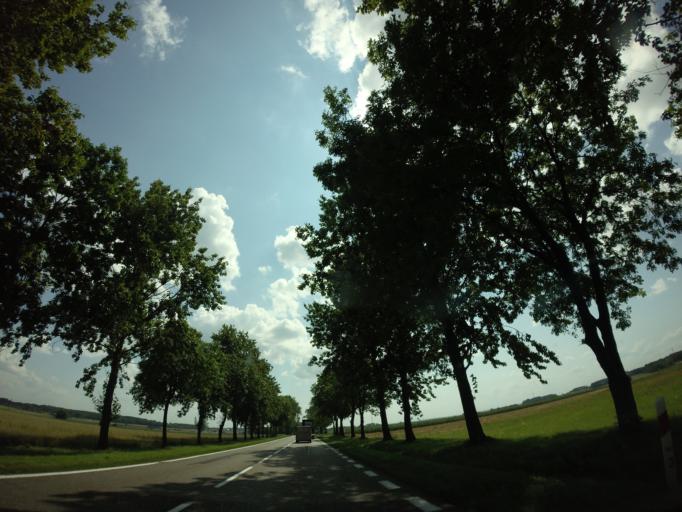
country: PL
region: Podlasie
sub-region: Powiat lomzynski
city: Piatnica
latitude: 53.2646
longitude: 22.1277
